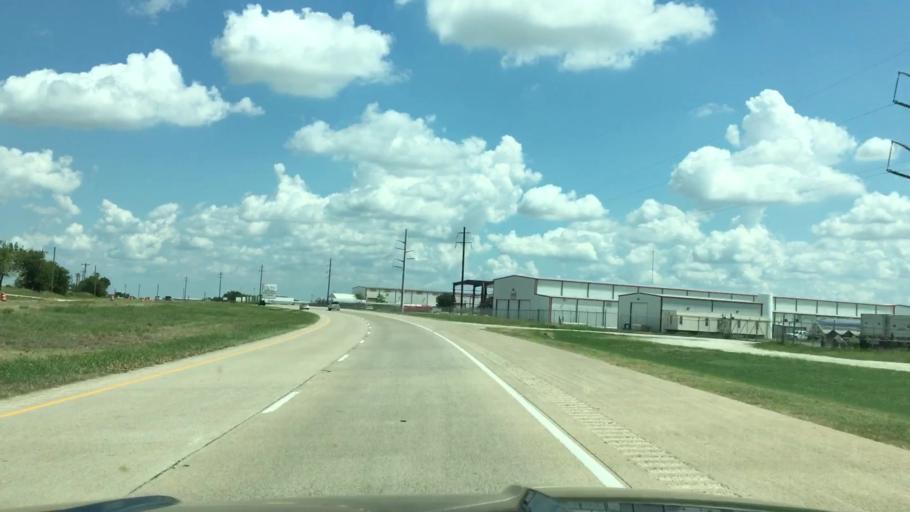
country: US
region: Texas
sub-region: Wise County
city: Rhome
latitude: 33.0374
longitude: -97.4413
